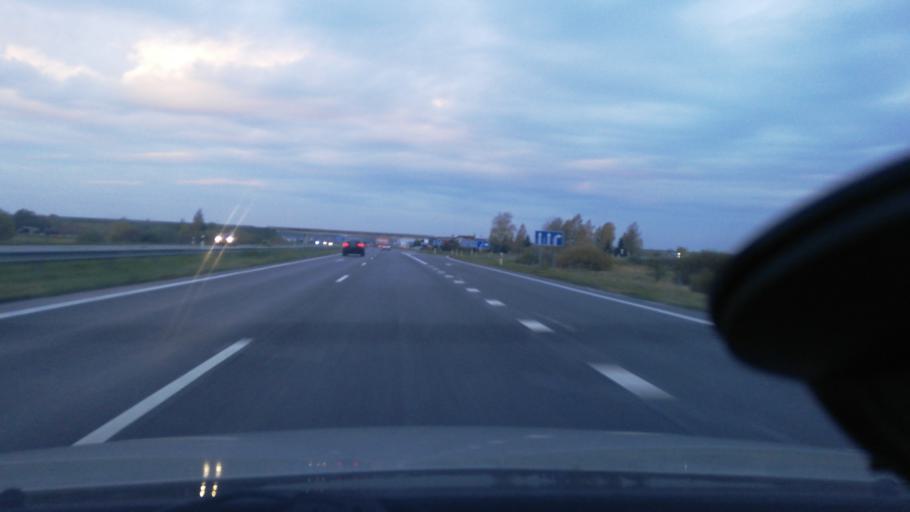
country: LT
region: Klaipedos apskritis
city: Gargzdai
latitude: 55.7326
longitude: 21.3885
